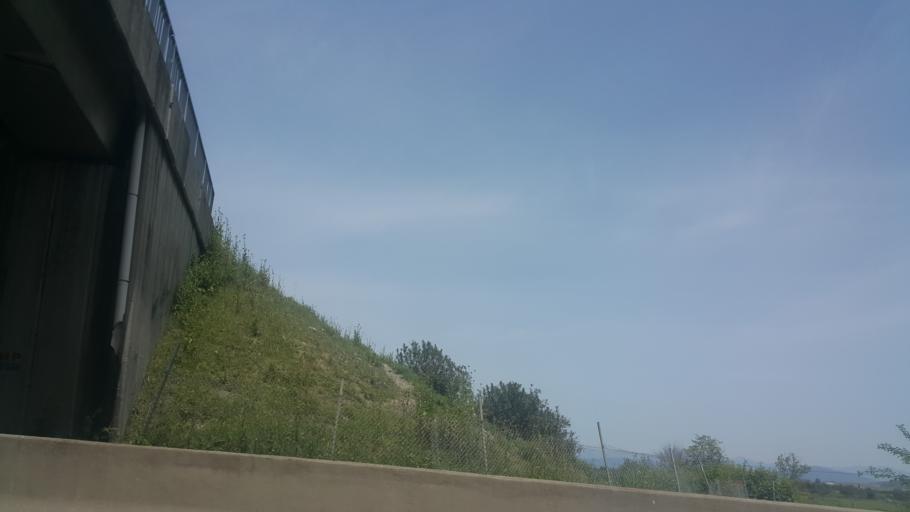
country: TR
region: Osmaniye
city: Toprakkale
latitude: 37.0624
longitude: 36.1104
